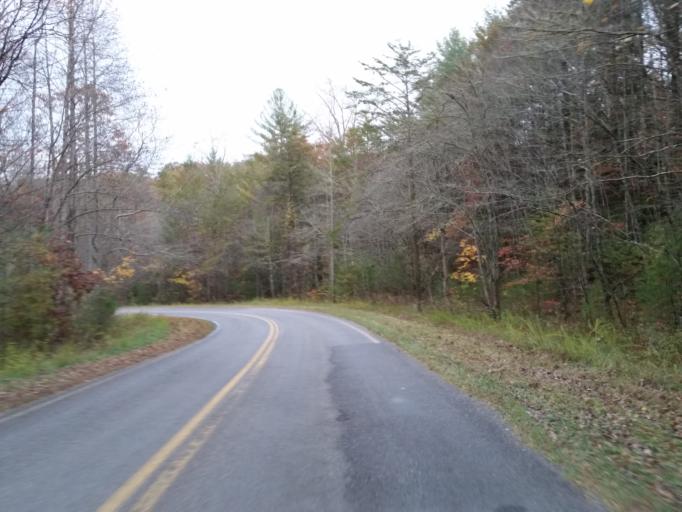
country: US
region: Georgia
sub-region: Fannin County
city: Blue Ridge
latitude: 34.6909
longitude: -84.2553
